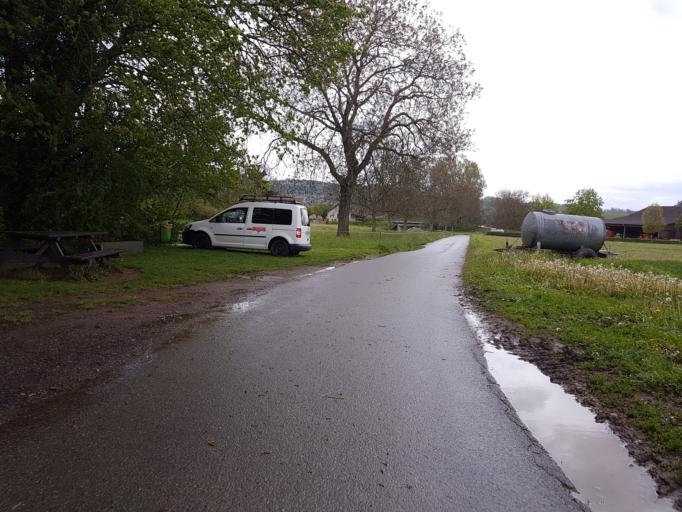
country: CH
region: Vaud
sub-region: Morges District
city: Orny
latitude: 46.6492
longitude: 6.5271
